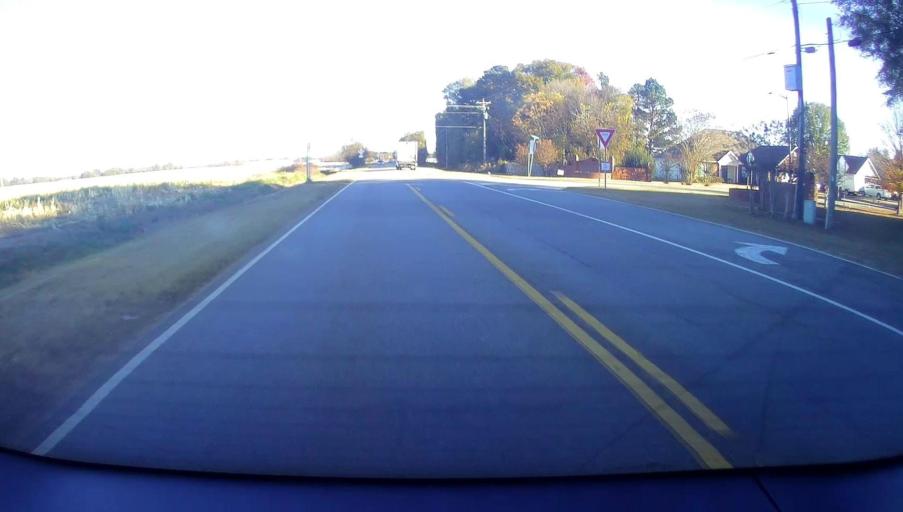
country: US
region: Georgia
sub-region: Houston County
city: Centerville
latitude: 32.5853
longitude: -83.7198
